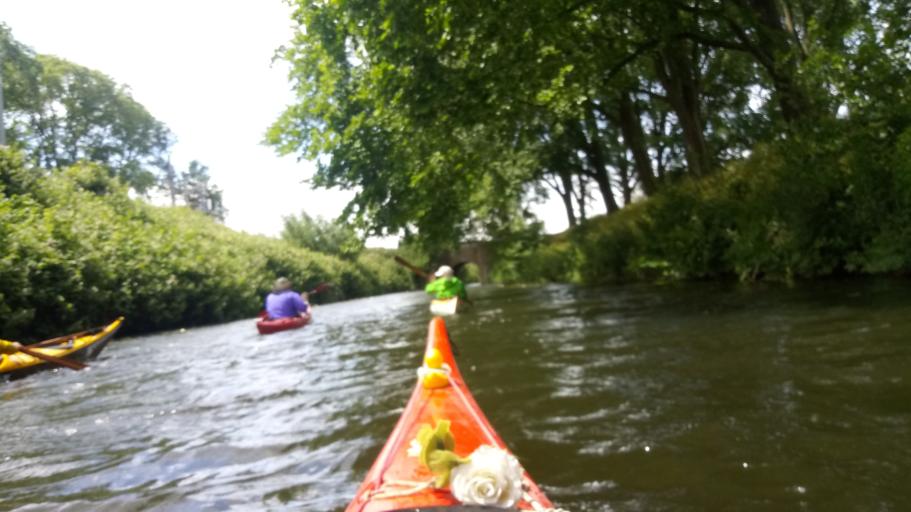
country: NL
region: North Holland
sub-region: Gemeente Enkhuizen
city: Enkhuizen
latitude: 52.6987
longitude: 5.2763
